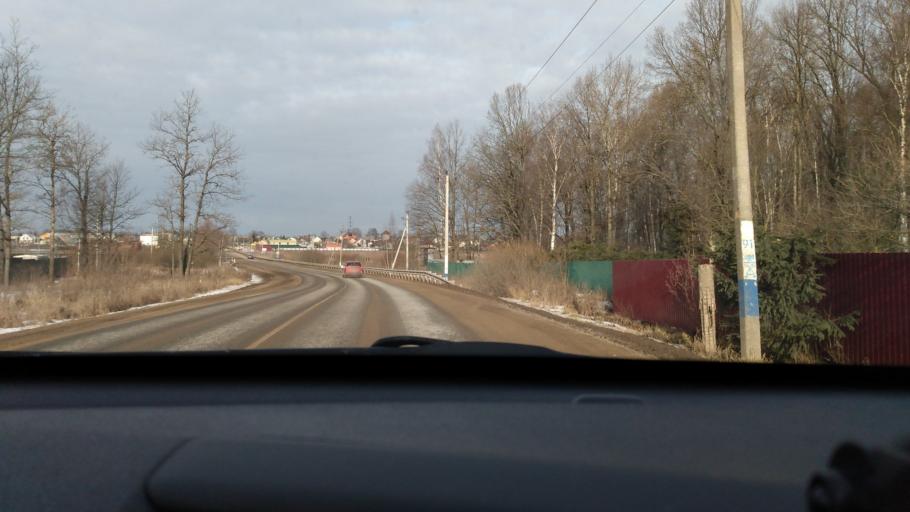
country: RU
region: Moskovskaya
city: Nakhabino
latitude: 55.8860
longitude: 37.1876
